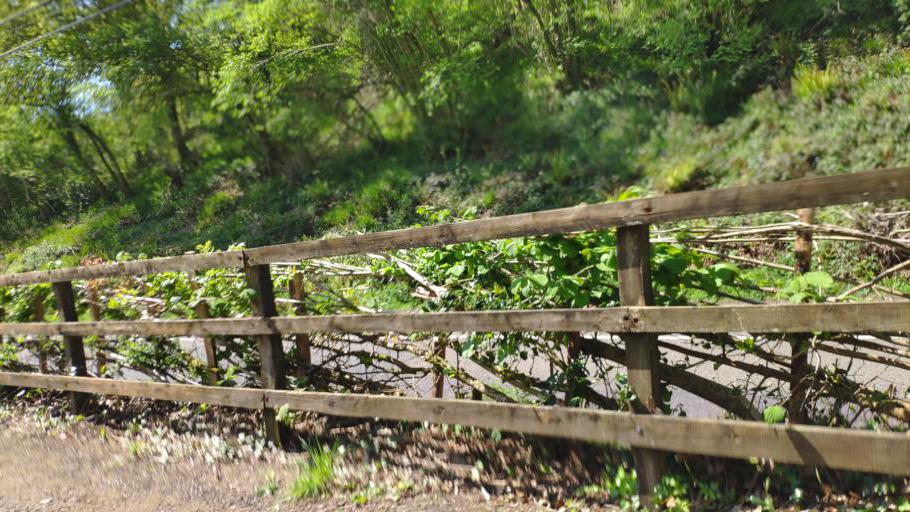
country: IE
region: Munster
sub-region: County Cork
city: Blarney
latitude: 51.9447
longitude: -8.5663
